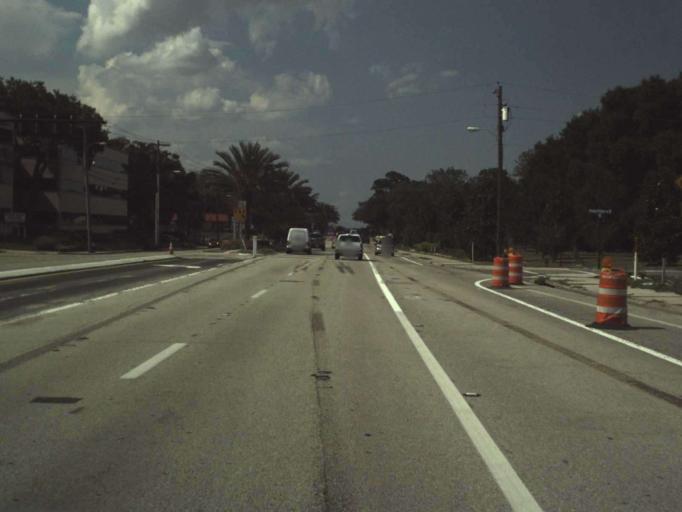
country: US
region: Florida
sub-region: Seminole County
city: Casselberry
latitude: 28.6650
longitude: -81.3400
